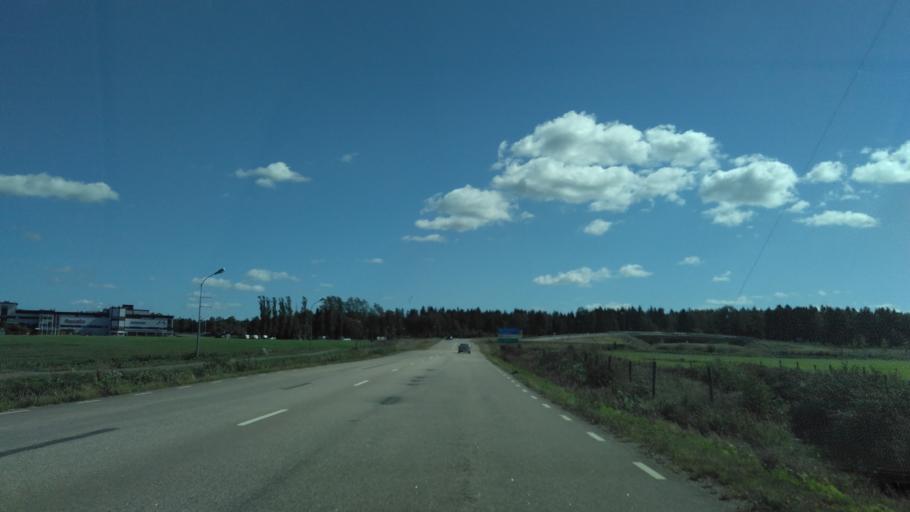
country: SE
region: Vaestra Goetaland
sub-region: Skara Kommun
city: Axvall
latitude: 58.3992
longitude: 13.5572
